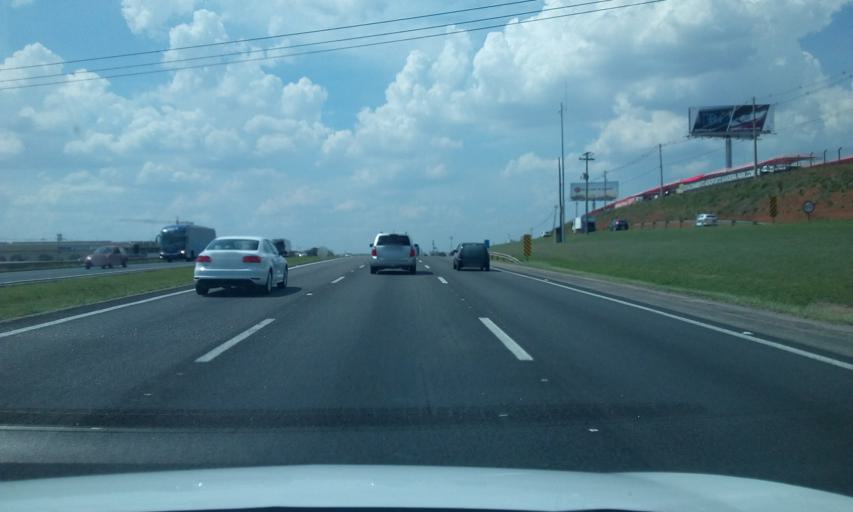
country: BR
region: Sao Paulo
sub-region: Campinas
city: Campinas
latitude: -23.0112
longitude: -47.1160
